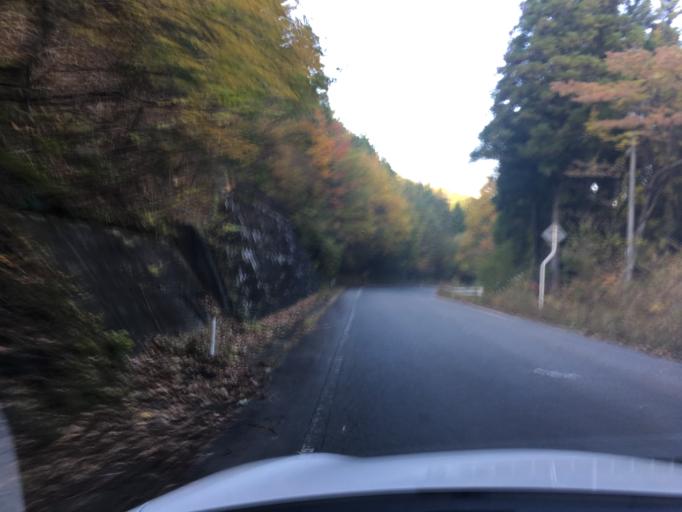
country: JP
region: Fukushima
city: Funehikimachi-funehiki
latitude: 37.2841
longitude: 140.7615
